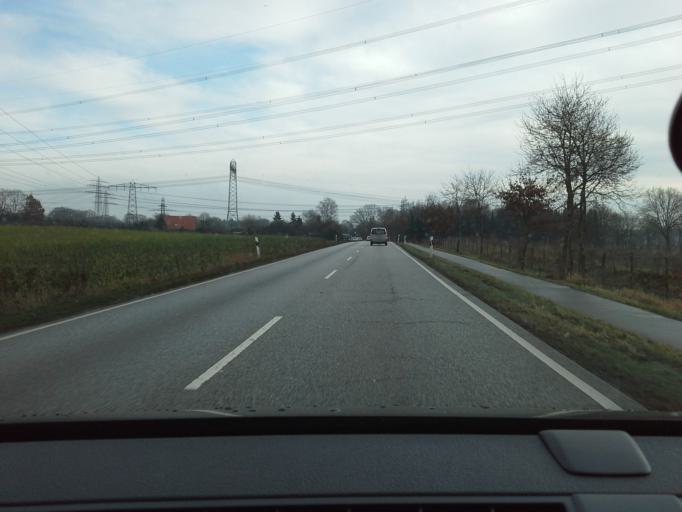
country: DE
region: Schleswig-Holstein
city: Ellerau
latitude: 53.7386
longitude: 9.9638
